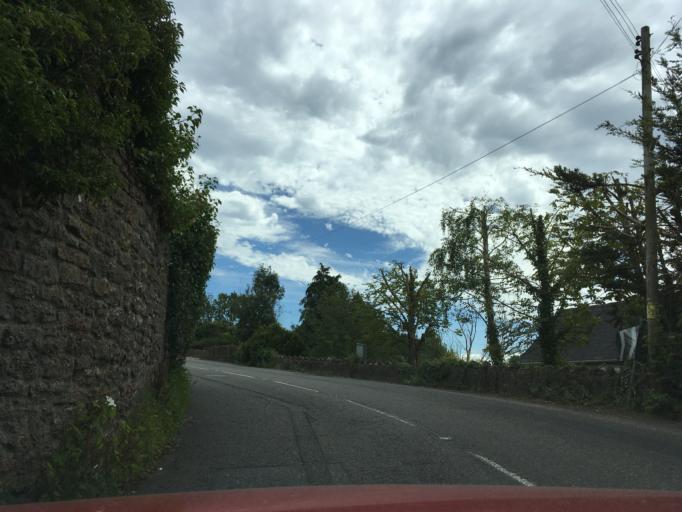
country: GB
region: England
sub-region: Somerset
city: Bradley Cross
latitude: 51.2465
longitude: -2.7371
